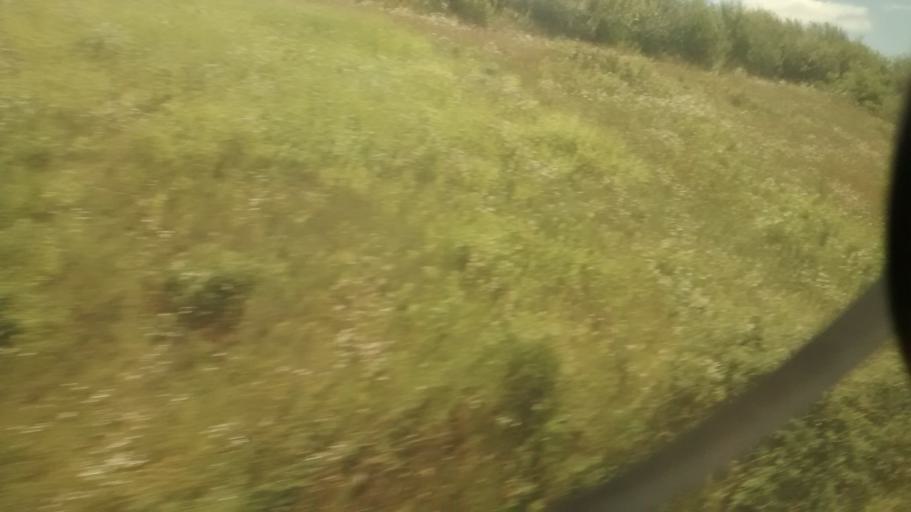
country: FR
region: Rhone-Alpes
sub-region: Departement de l'Ain
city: Beynost
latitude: 45.8528
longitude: 5.0011
